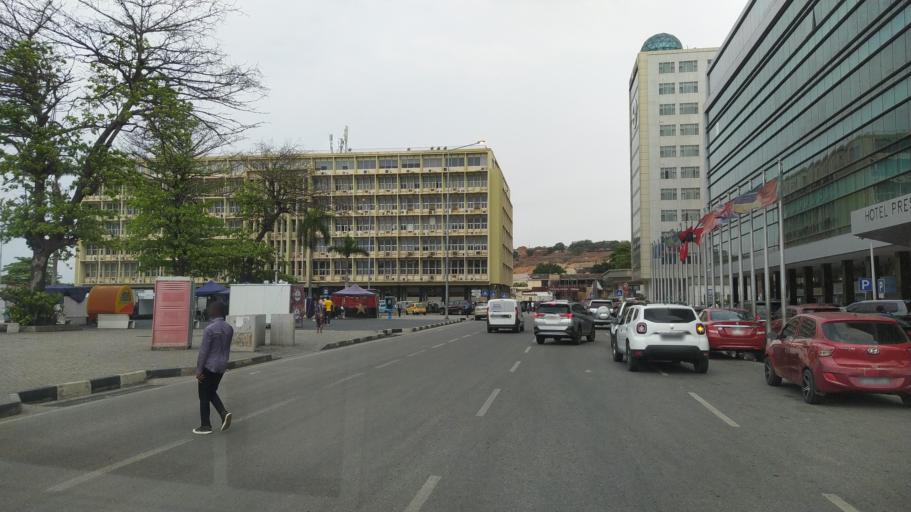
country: AO
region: Luanda
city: Luanda
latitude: -8.8032
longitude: 13.2420
